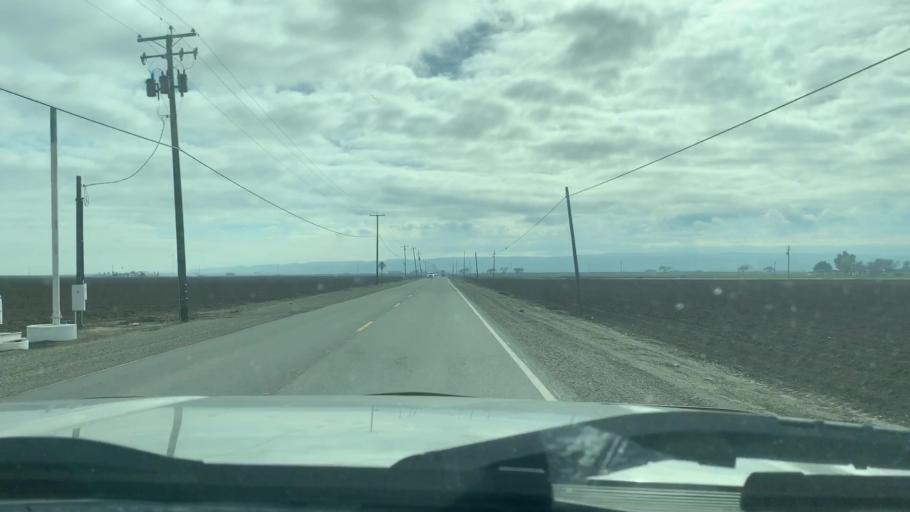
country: US
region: California
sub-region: Merced County
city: Los Banos
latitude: 36.9932
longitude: -120.8372
